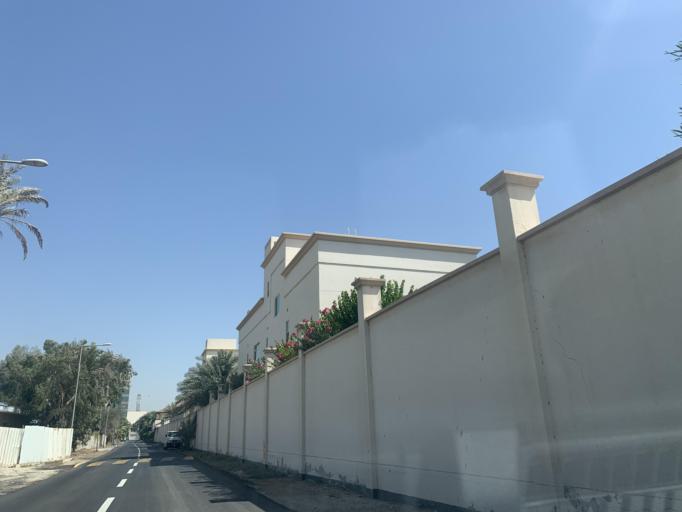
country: BH
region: Manama
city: Jidd Hafs
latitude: 26.2247
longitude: 50.5009
